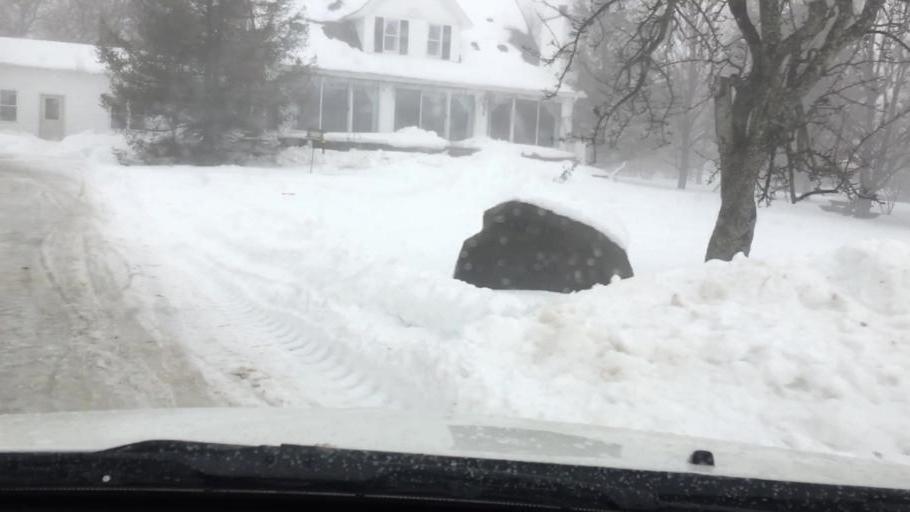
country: US
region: Michigan
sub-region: Charlevoix County
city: East Jordan
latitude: 45.1200
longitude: -85.1802
